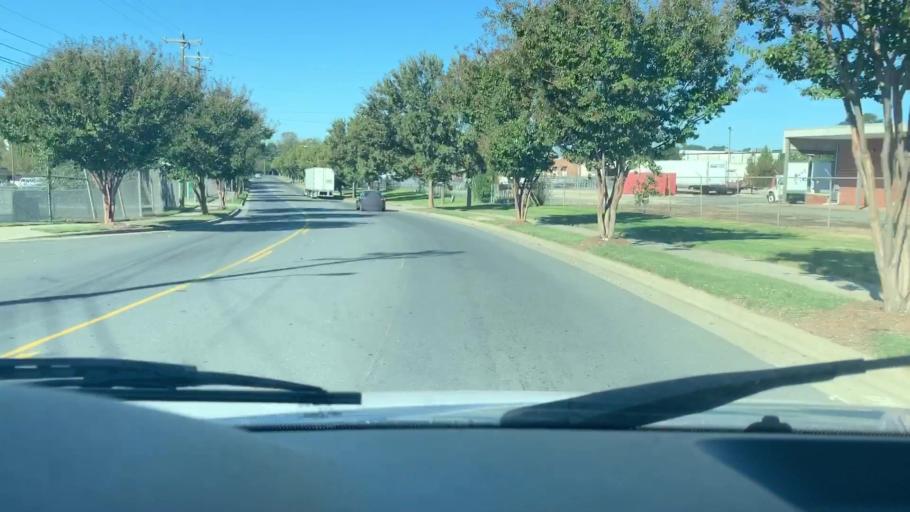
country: US
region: North Carolina
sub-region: Mecklenburg County
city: Charlotte
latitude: 35.2616
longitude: -80.8212
